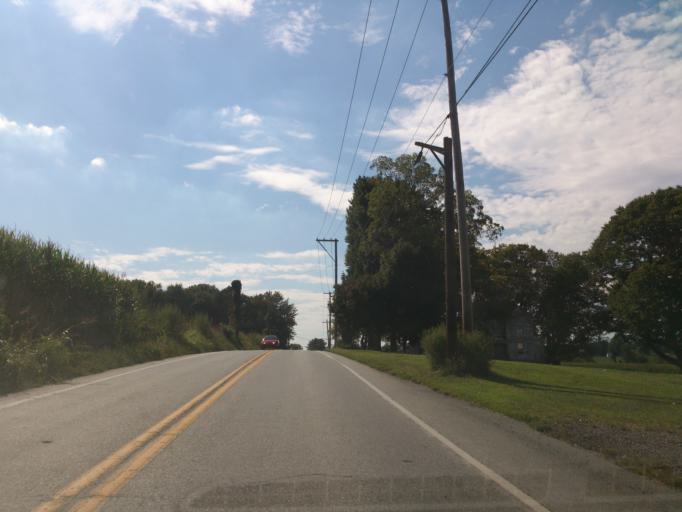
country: US
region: Pennsylvania
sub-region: York County
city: Windsor
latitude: 39.8811
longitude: -76.5331
